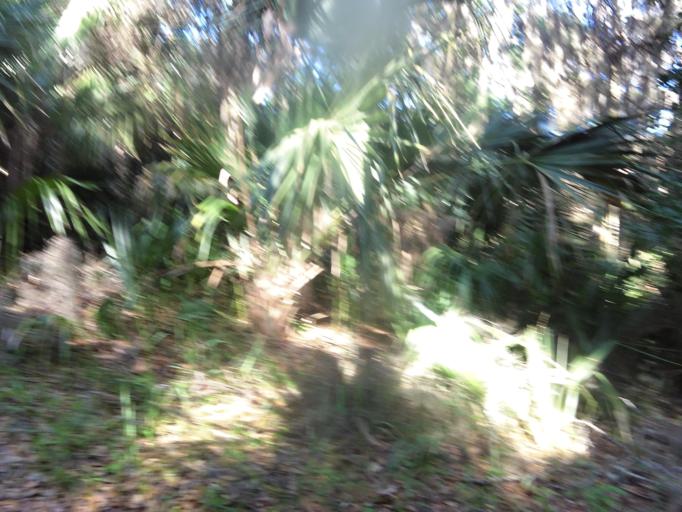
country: US
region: Florida
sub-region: Duval County
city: Atlantic Beach
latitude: 30.4424
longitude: -81.4693
